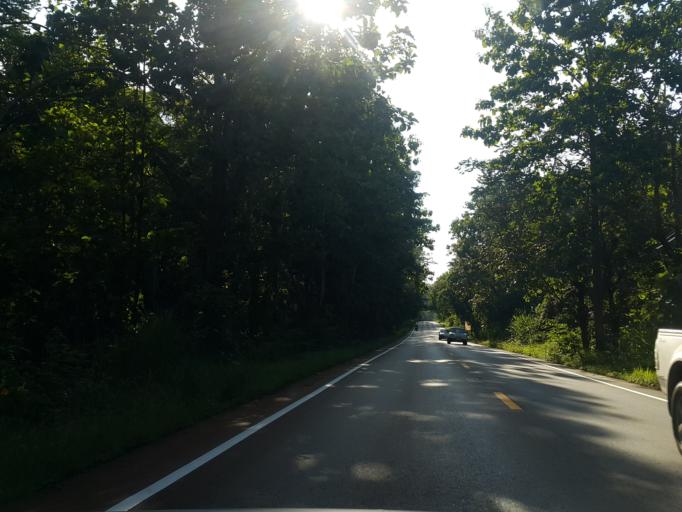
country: TH
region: Chiang Mai
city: Mae Taeng
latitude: 19.0746
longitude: 99.1177
